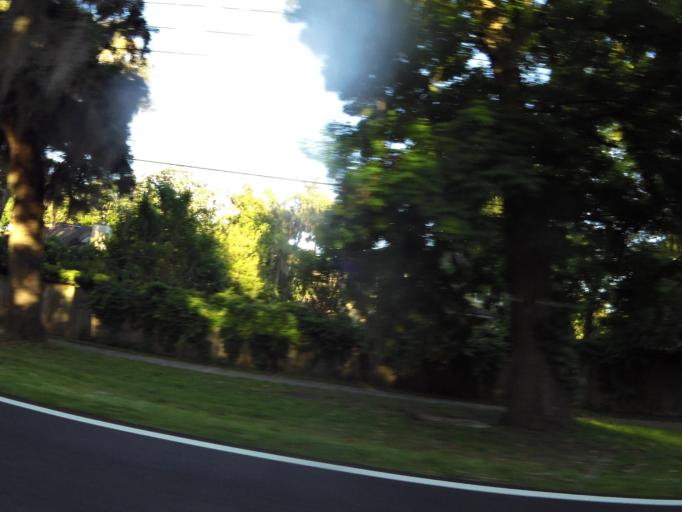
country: US
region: Florida
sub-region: Duval County
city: Atlantic Beach
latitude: 30.3730
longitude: -81.5131
